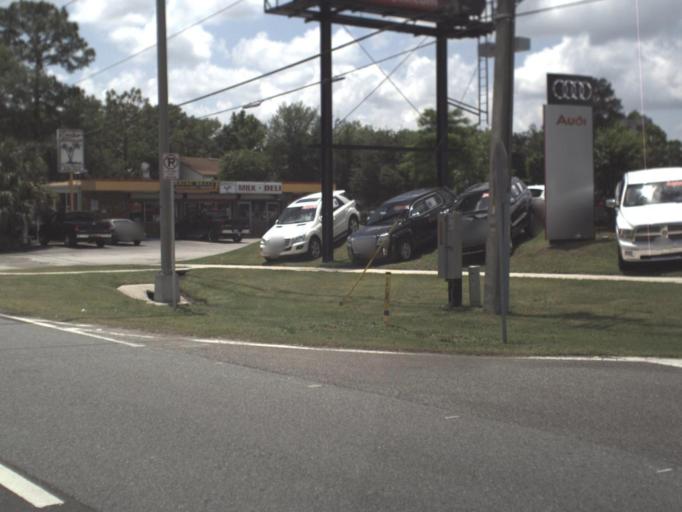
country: US
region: Florida
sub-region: Clay County
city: Bellair-Meadowbrook Terrace
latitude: 30.2153
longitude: -81.7372
